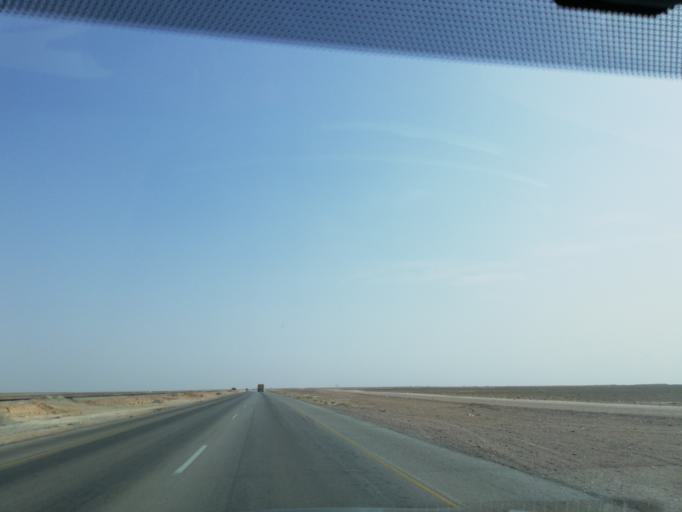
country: OM
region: Muhafazat ad Dakhiliyah
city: Adam
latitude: 21.6018
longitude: 57.2956
